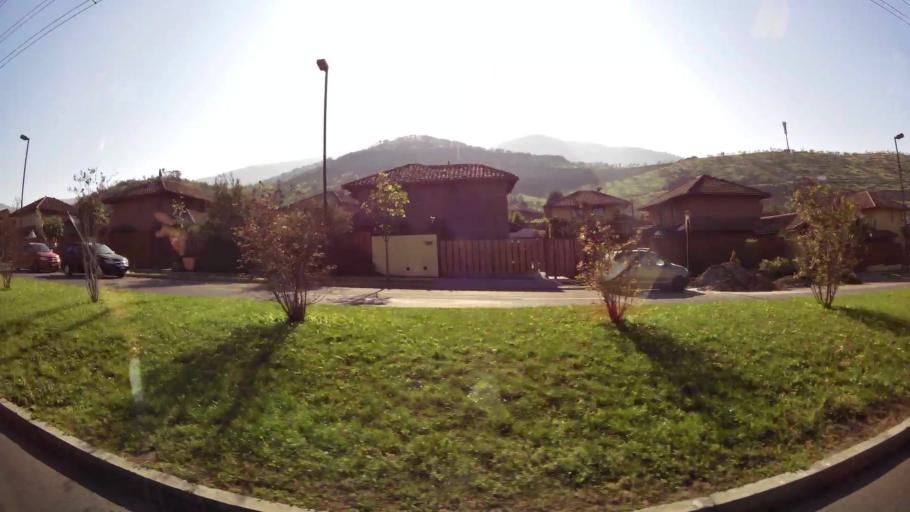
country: CL
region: Santiago Metropolitan
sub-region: Provincia de Chacabuco
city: Chicureo Abajo
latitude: -33.3508
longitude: -70.6648
